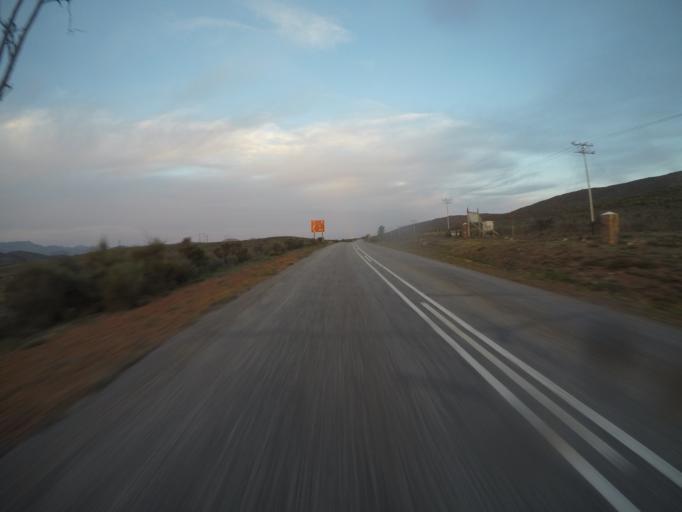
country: ZA
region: Western Cape
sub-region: Eden District Municipality
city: Plettenberg Bay
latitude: -33.7410
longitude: 23.4380
